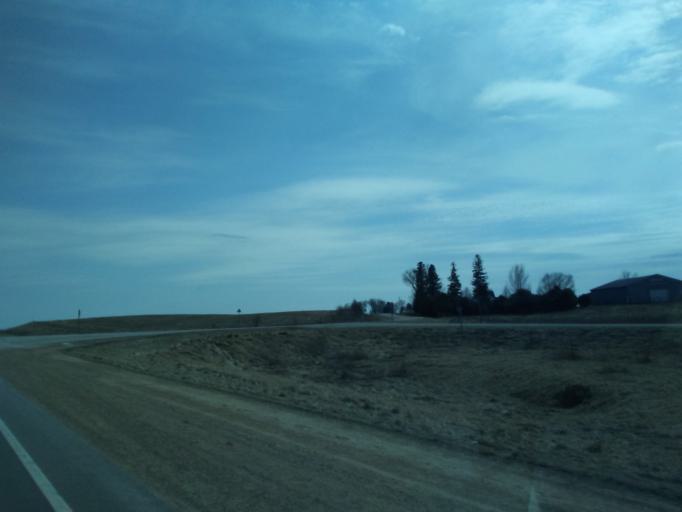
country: US
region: Iowa
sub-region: Winneshiek County
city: Decorah
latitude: 43.3852
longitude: -91.8250
